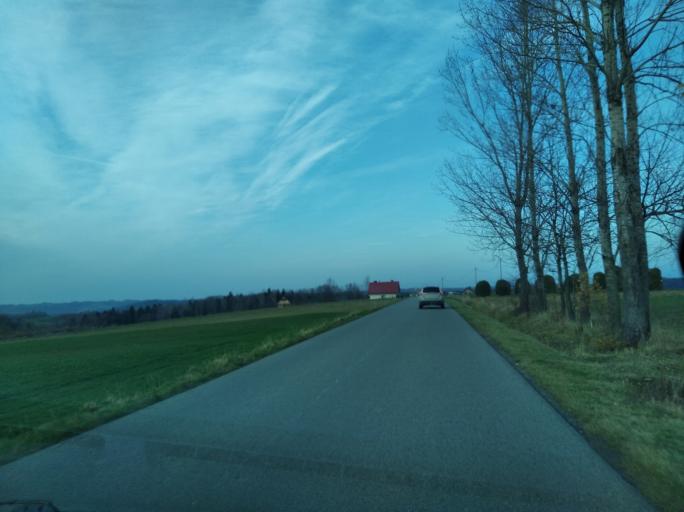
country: PL
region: Subcarpathian Voivodeship
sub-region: Powiat ropczycko-sedziszowski
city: Zagorzyce
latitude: 49.9821
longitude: 21.7137
